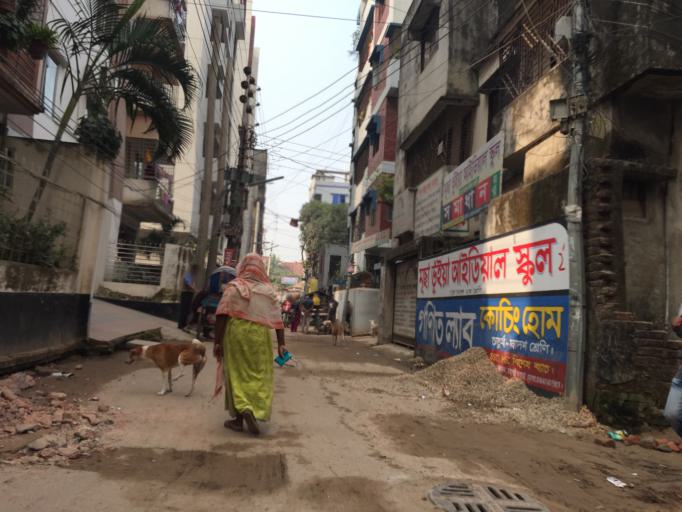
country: BD
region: Dhaka
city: Azimpur
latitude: 23.7882
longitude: 90.3607
